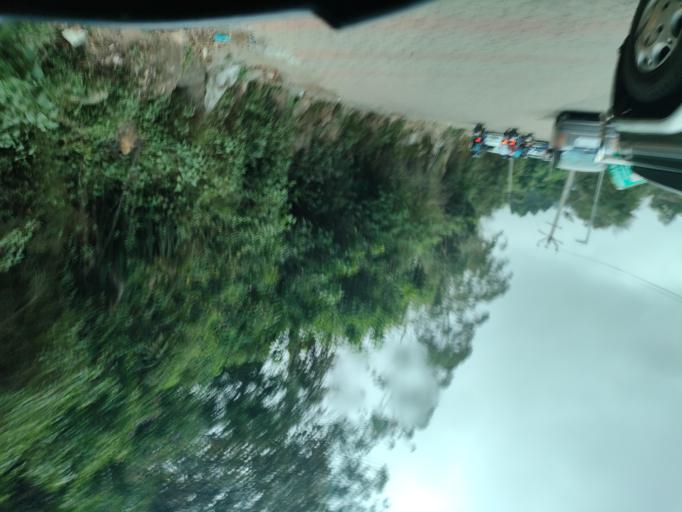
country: IN
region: Tamil Nadu
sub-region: Dindigul
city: Kodaikanal
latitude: 10.2401
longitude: 77.5102
